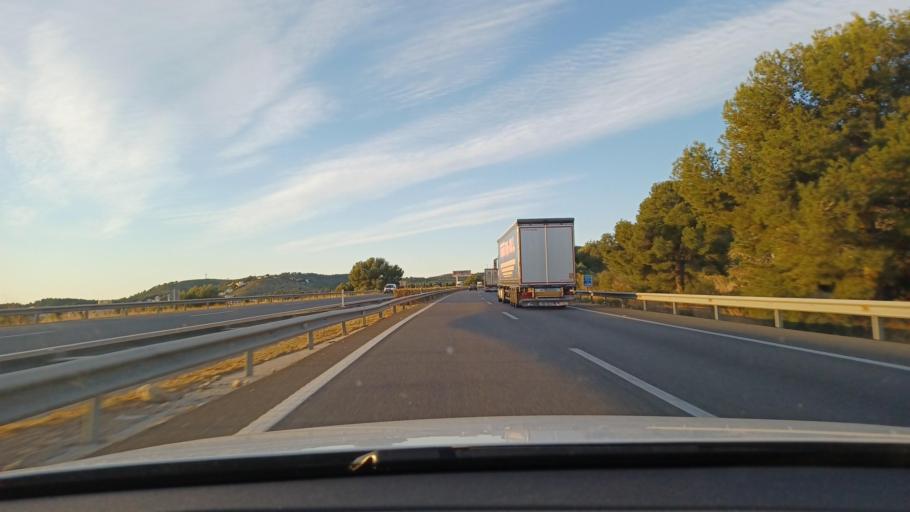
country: ES
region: Valencia
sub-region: Provincia de Castello
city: Orpesa/Oropesa del Mar
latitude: 40.0994
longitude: 0.1287
